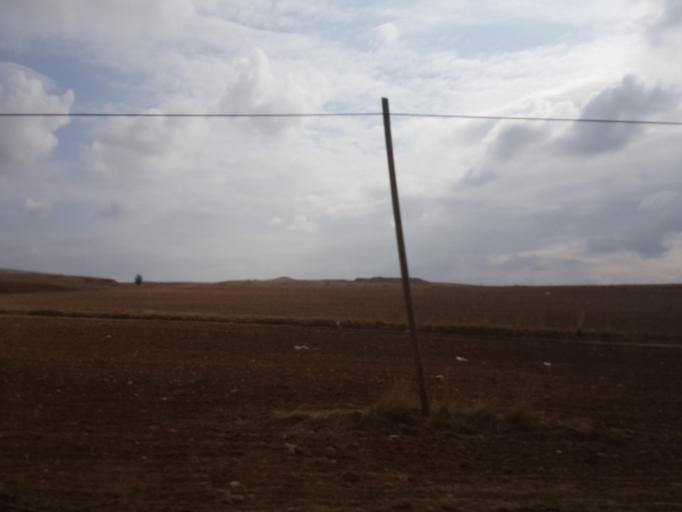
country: TR
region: Kirikkale
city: Keskin
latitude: 39.5828
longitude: 33.5967
